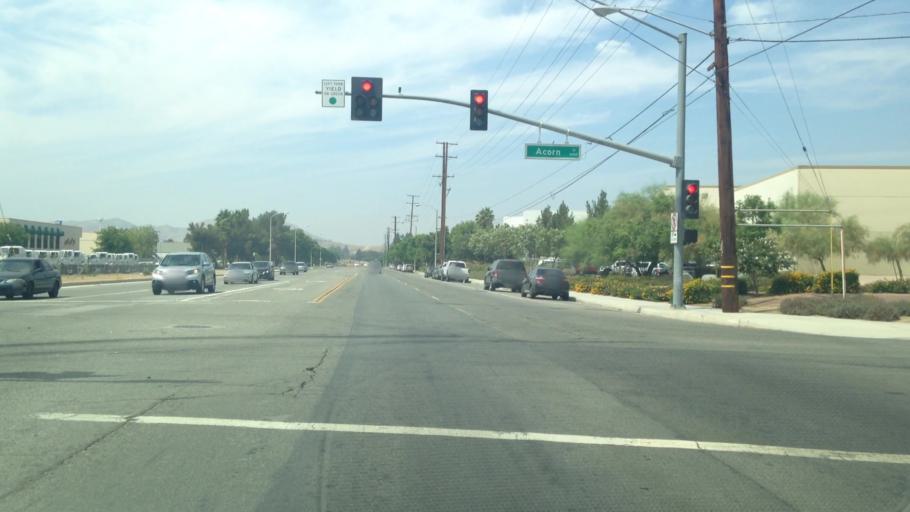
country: US
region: California
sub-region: Riverside County
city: Pedley
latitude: 33.9598
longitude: -117.4538
